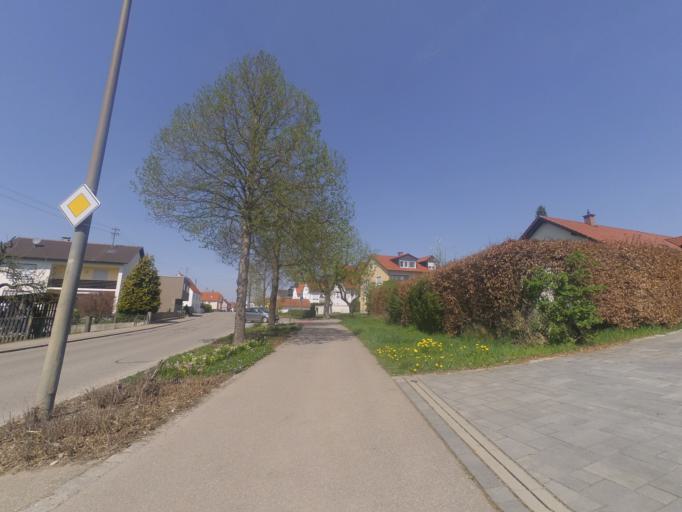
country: DE
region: Bavaria
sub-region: Swabia
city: Weissenhorn
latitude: 48.2924
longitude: 10.1613
